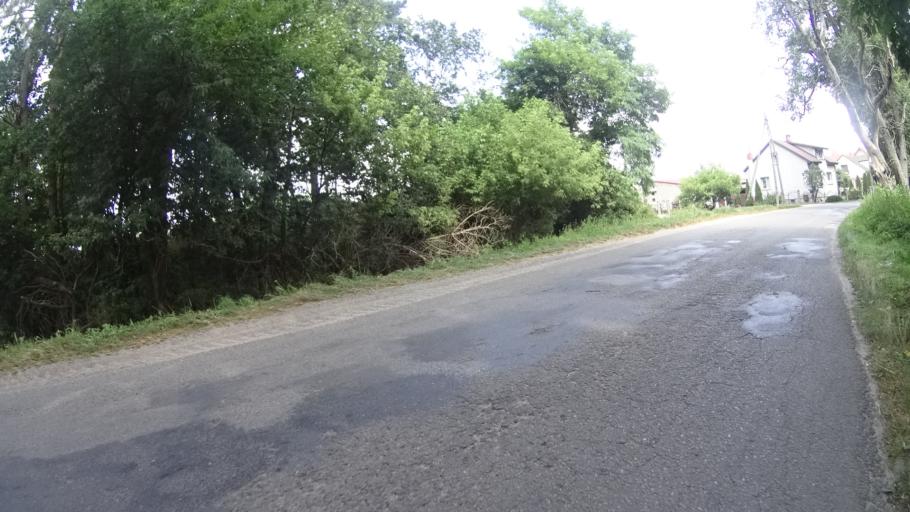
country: PL
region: Masovian Voivodeship
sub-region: Powiat bialobrzeski
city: Wysmierzyce
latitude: 51.6579
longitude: 20.7786
